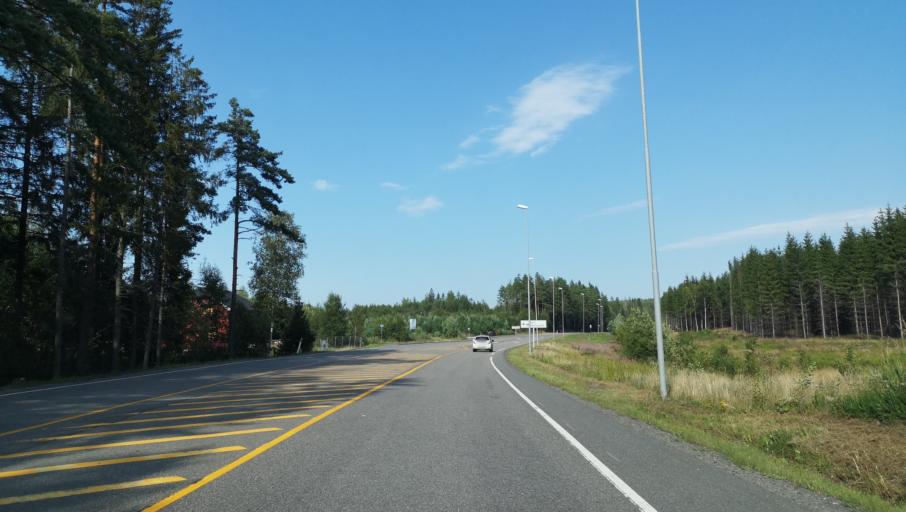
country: NO
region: Ostfold
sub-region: Valer
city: Kirkebygda
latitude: 59.4816
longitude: 10.7948
